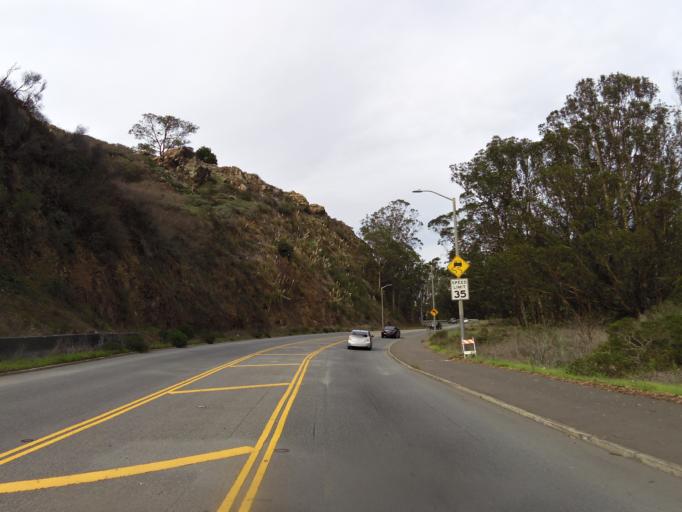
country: US
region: California
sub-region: San Mateo County
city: Daly City
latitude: 37.7379
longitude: -122.4424
